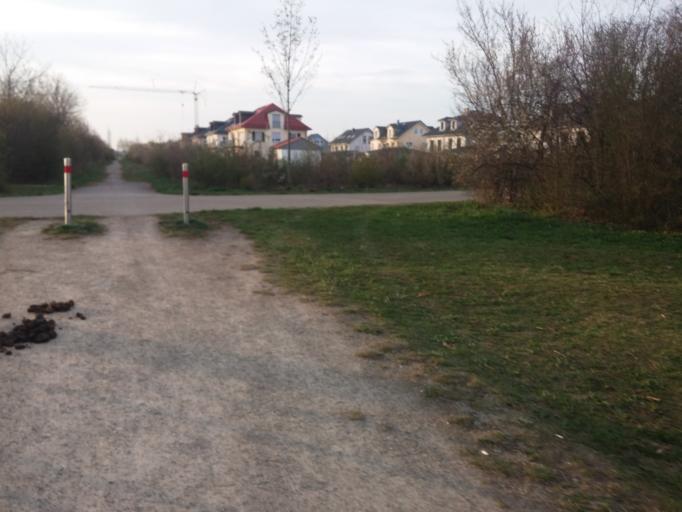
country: DE
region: Bavaria
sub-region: Upper Bavaria
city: Aschheim
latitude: 48.1635
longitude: 11.7125
